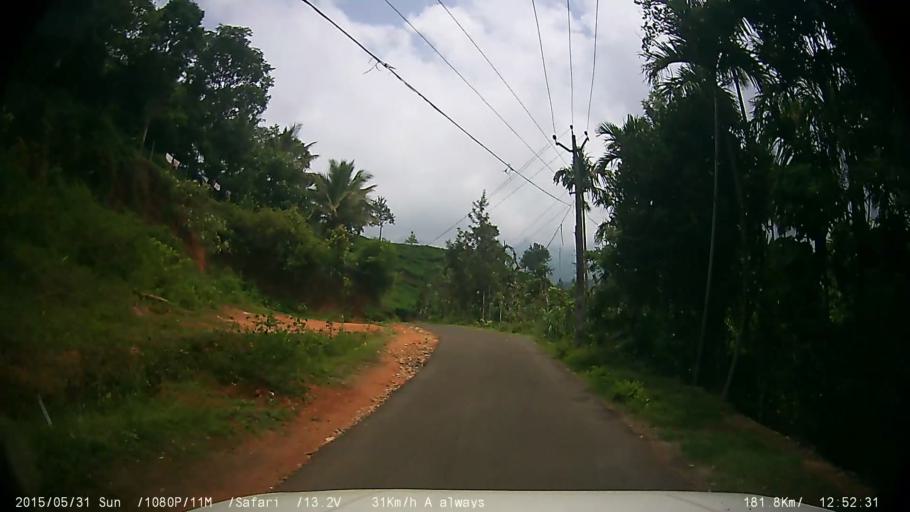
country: IN
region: Kerala
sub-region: Wayanad
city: Kalpetta
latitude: 11.5074
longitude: 76.1509
